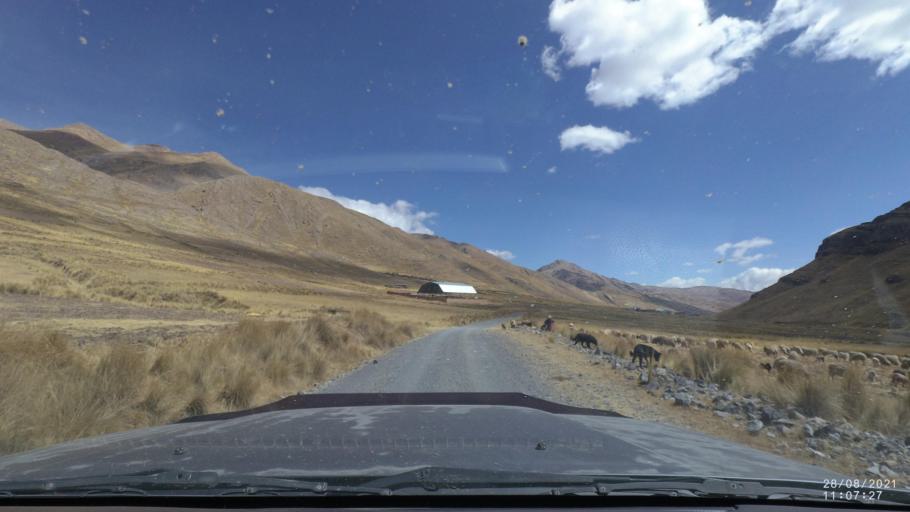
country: BO
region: Cochabamba
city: Cochabamba
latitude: -17.1709
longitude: -66.2992
